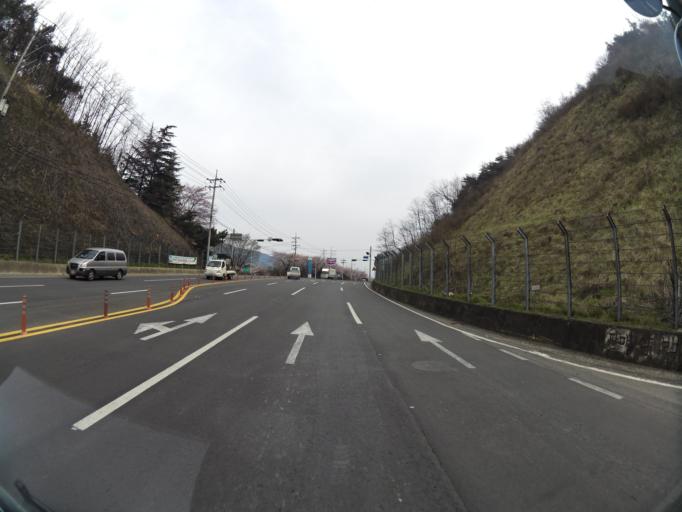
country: KR
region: Gyeongsangnam-do
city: Changnyeong
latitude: 35.4428
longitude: 128.5719
